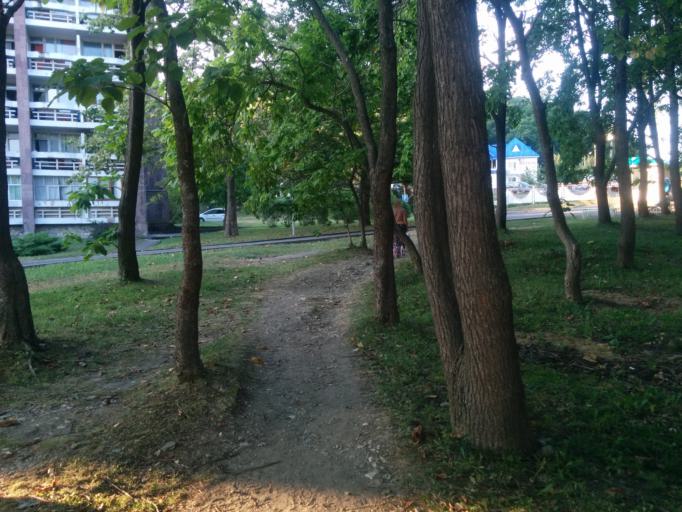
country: RU
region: Krasnodarskiy
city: Novomikhaylovskiy
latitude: 44.2599
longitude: 38.8214
